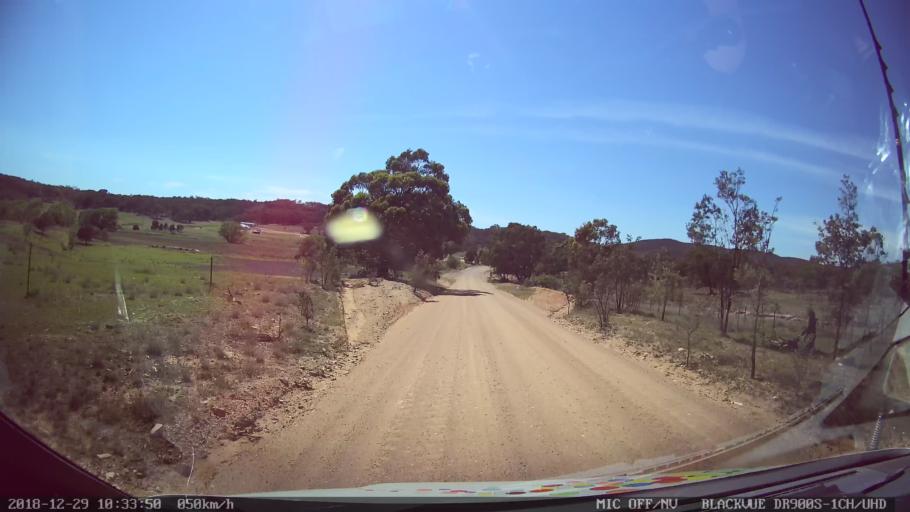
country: AU
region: New South Wales
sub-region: Yass Valley
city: Gundaroo
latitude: -34.9832
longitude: 149.4740
